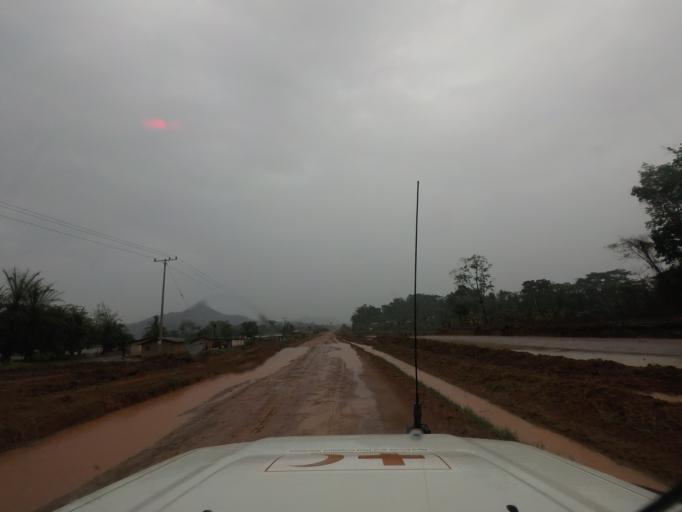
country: LR
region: Nimba
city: Sanniquellie
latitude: 7.2731
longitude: -8.8364
